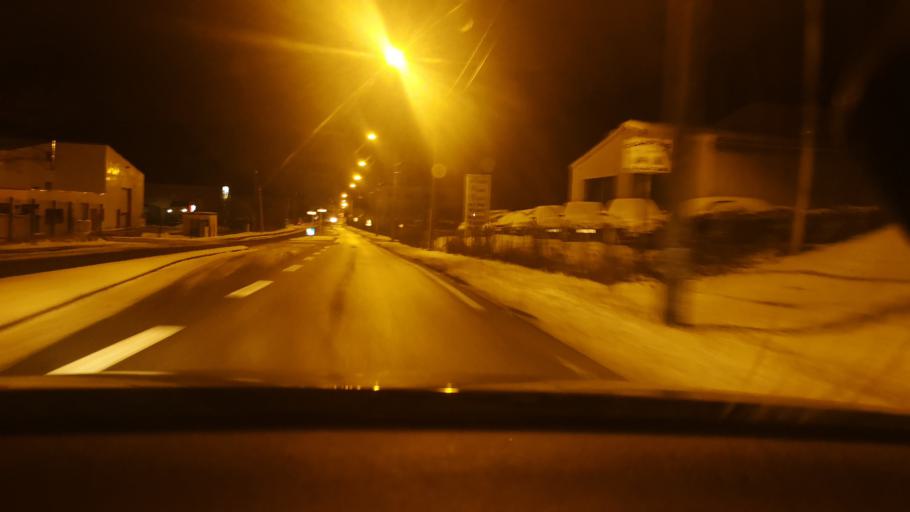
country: FR
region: Rhone-Alpes
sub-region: Departement de l'Ain
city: Nantua
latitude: 46.1439
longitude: 5.6159
